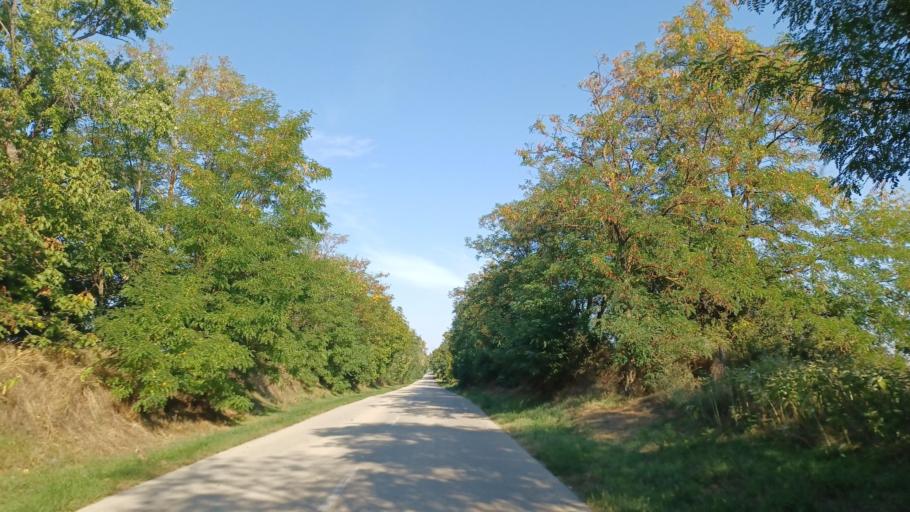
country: HU
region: Tolna
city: Dunaszentgyorgy
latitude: 46.5093
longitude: 18.7870
